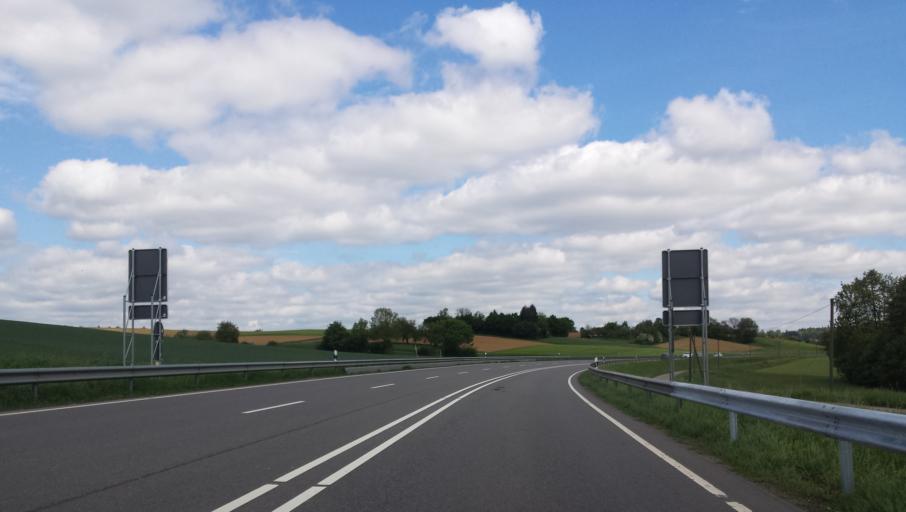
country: DE
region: Baden-Wuerttemberg
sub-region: Karlsruhe Region
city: Aglasterhausen
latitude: 49.3448
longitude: 8.9784
